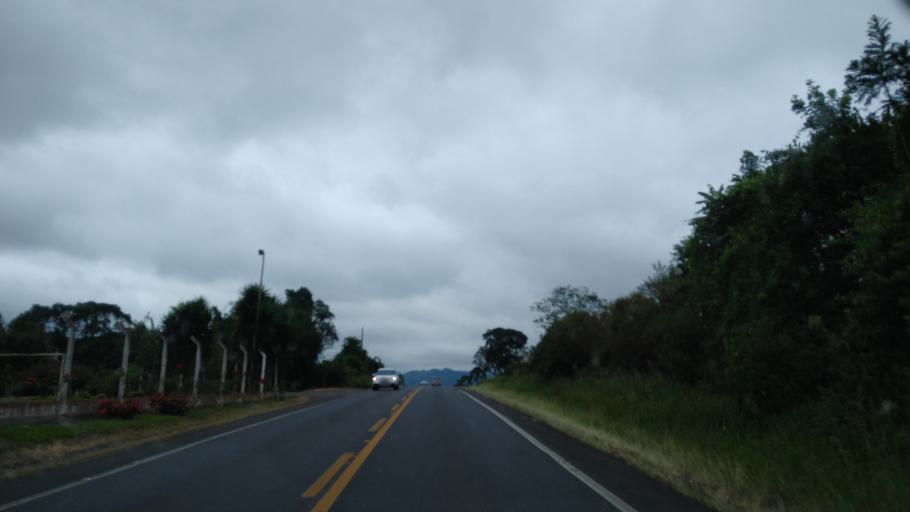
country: BR
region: Santa Catarina
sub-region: Porto Uniao
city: Porto Uniao
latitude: -26.2822
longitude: -51.0038
